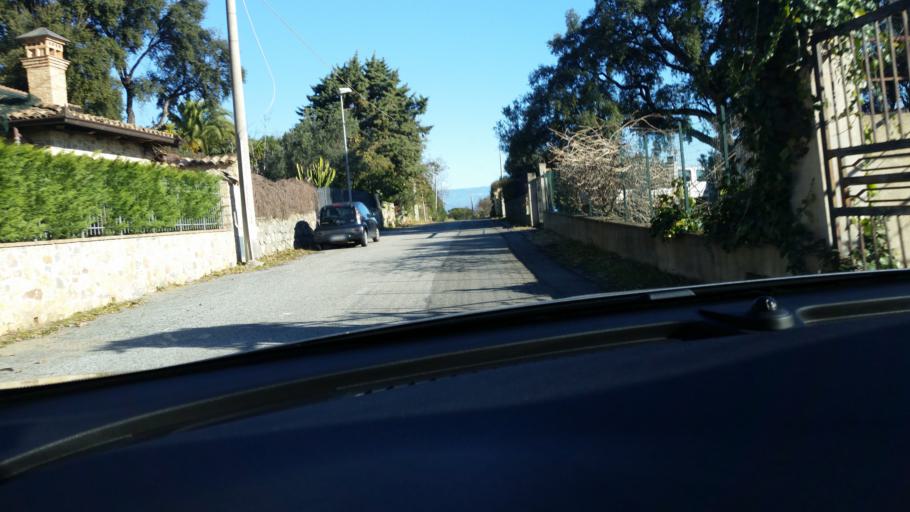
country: IT
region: Calabria
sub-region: Provincia di Catanzaro
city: Squillace Lido
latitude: 38.7598
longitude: 16.5671
